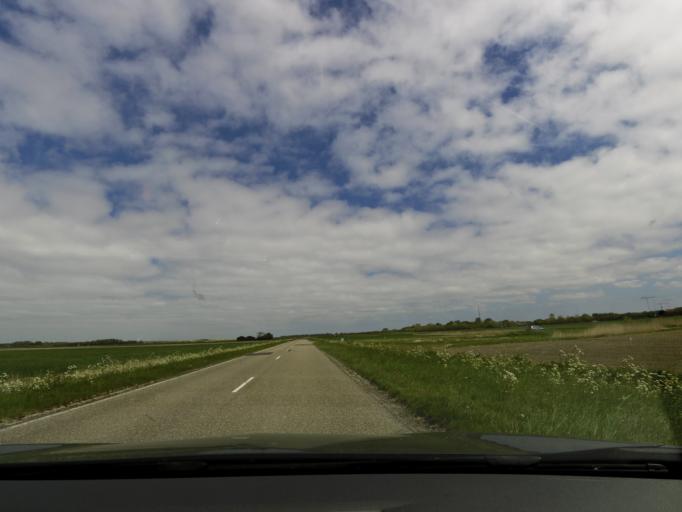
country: NL
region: South Holland
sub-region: Gemeente Goeree-Overflakkee
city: Ouddorp
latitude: 51.8103
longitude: 3.8794
